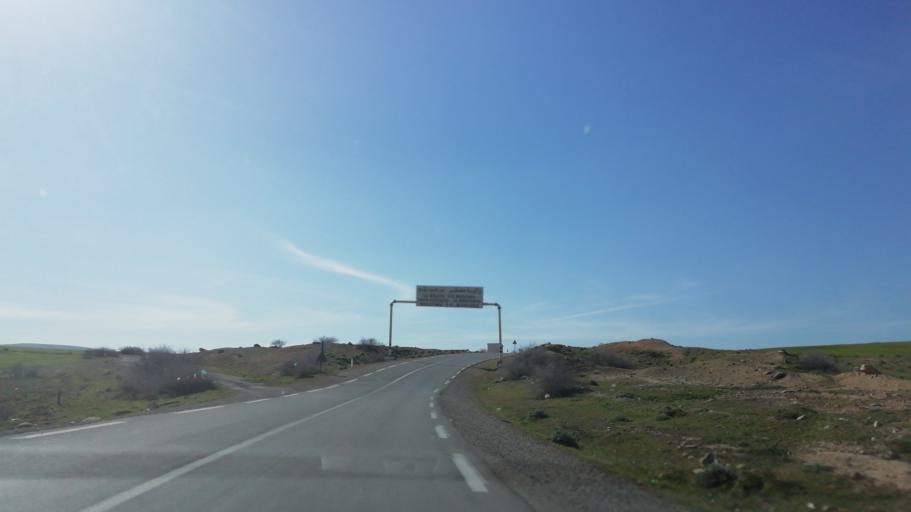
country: DZ
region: Mascara
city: Oued el Abtal
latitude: 35.4443
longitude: 0.8292
